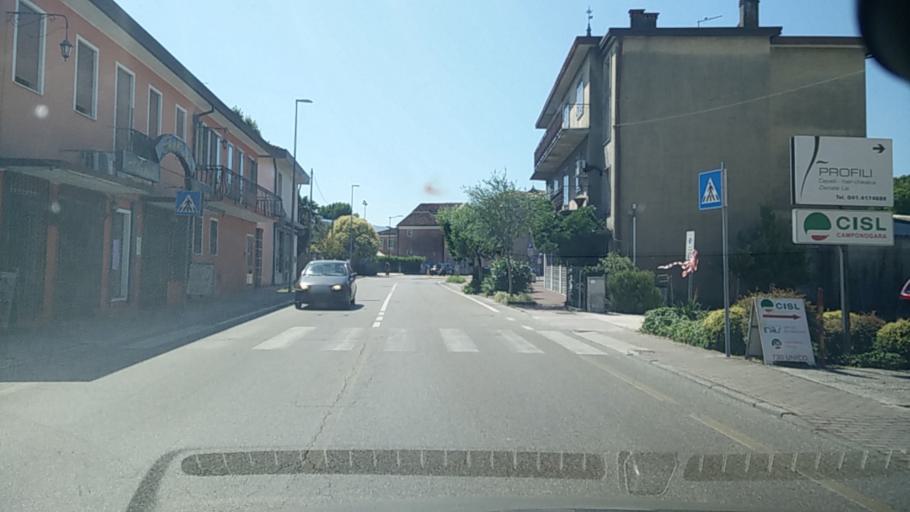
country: IT
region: Veneto
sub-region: Provincia di Venezia
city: Camponogara
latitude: 45.3871
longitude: 12.0717
